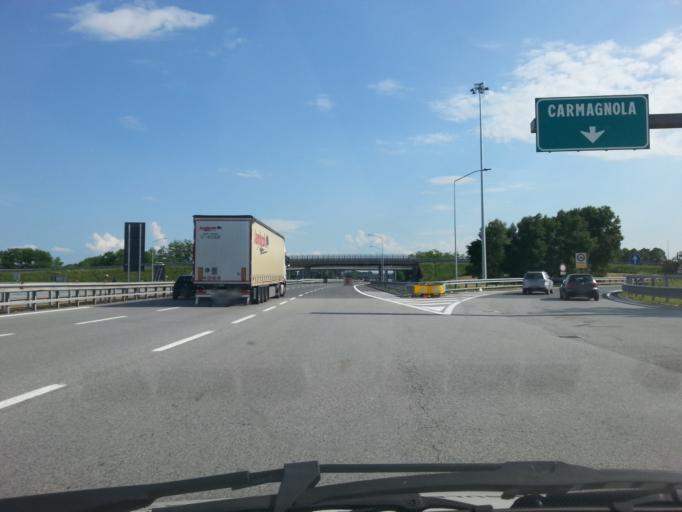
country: IT
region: Piedmont
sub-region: Provincia di Torino
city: Carmagnola
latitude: 44.8536
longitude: 7.7483
